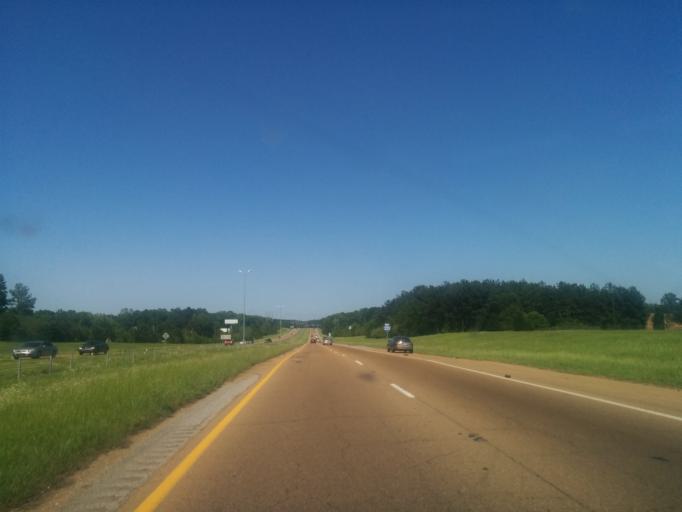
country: US
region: Mississippi
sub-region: Madison County
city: Ridgeland
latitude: 32.4013
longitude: -90.1751
